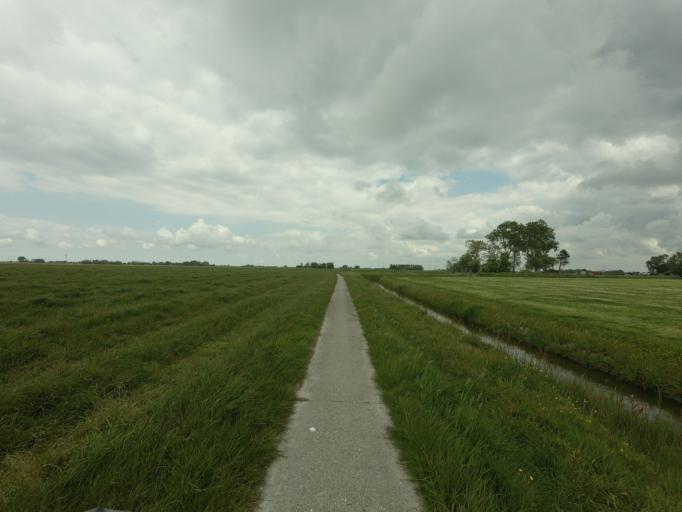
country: NL
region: Friesland
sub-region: Gemeente Littenseradiel
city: Wommels
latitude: 53.1097
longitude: 5.6099
